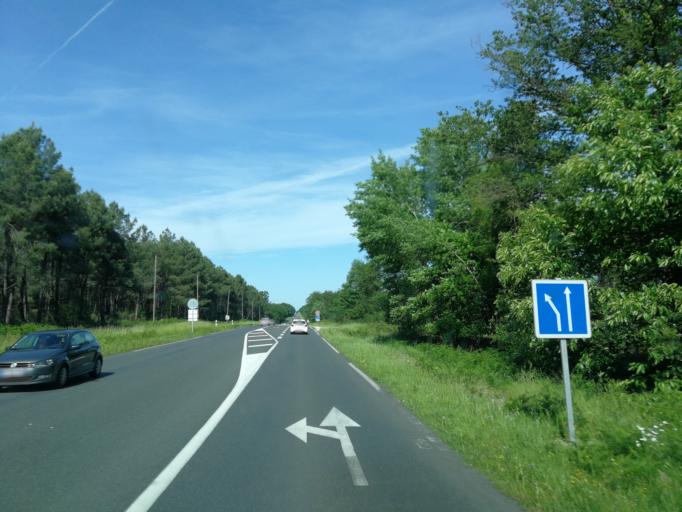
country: FR
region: Centre
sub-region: Departement d'Indre-et-Loire
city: Cheille
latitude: 47.2090
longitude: 0.3430
